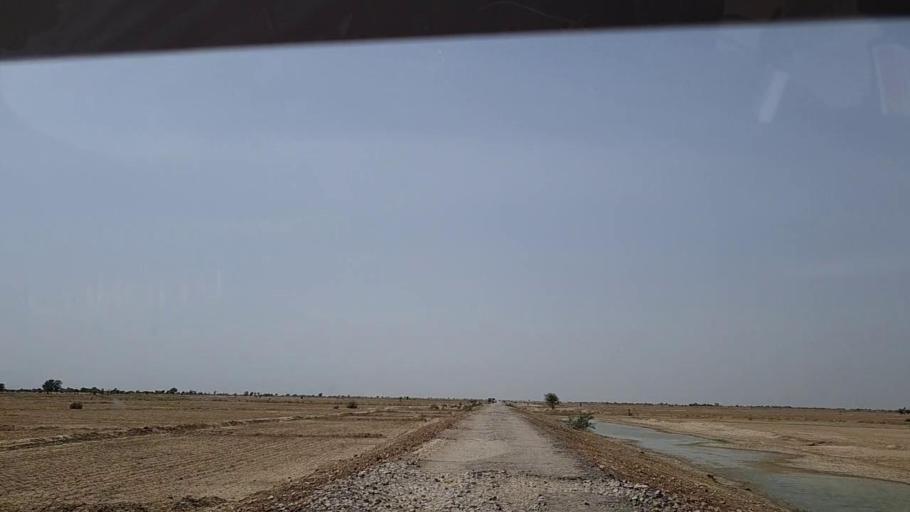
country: PK
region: Sindh
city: Johi
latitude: 26.7199
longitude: 67.6458
